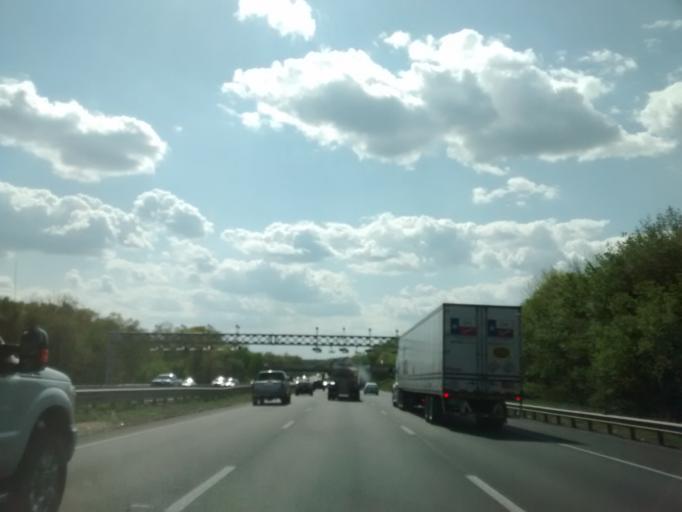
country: US
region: Massachusetts
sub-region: Worcester County
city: Charlton
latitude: 42.1533
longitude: -71.9748
